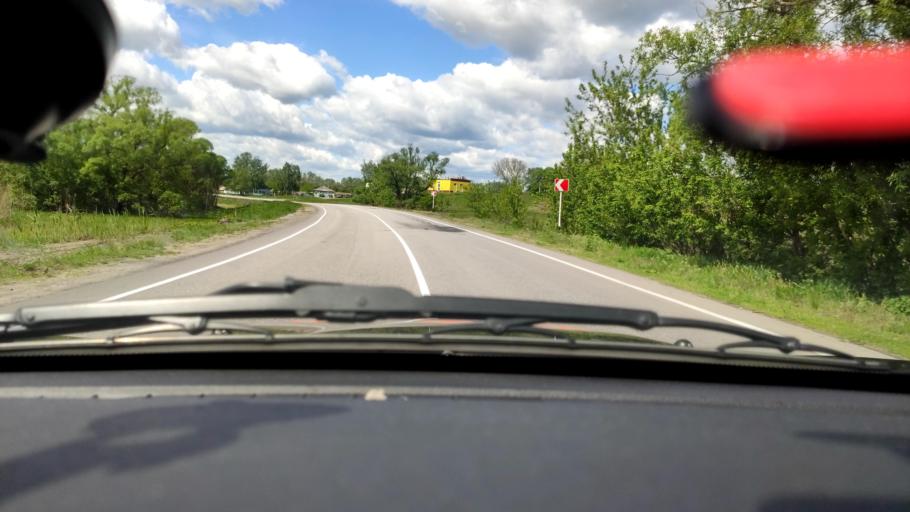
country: RU
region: Voronezj
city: Ostrogozhsk
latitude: 51.0554
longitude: 38.9219
